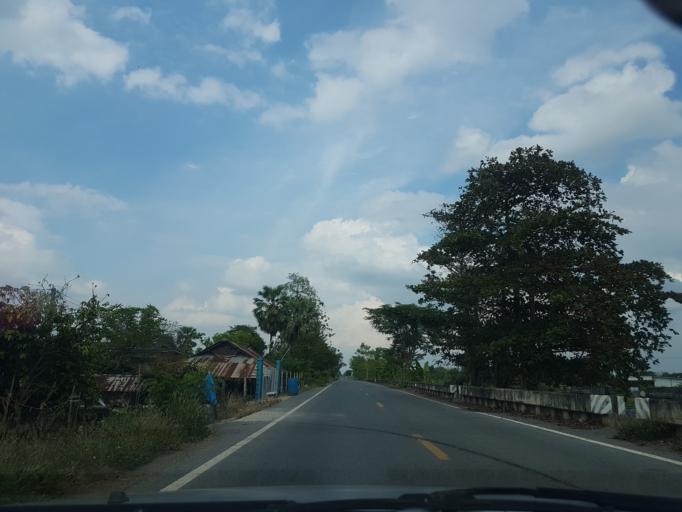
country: TH
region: Pathum Thani
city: Nong Suea
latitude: 14.1992
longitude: 100.8915
